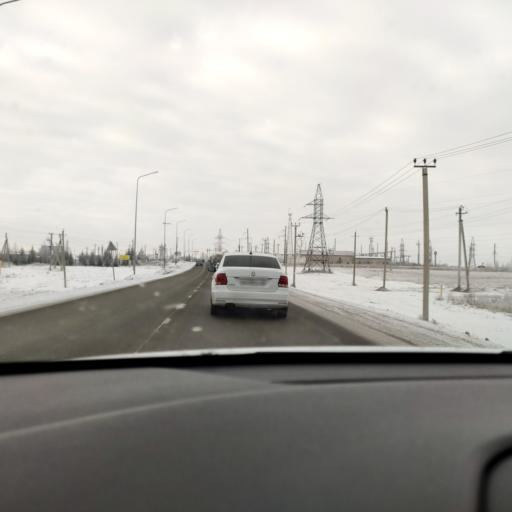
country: RU
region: Tatarstan
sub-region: Arskiy Rayon
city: Arsk
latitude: 56.1053
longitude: 49.8793
